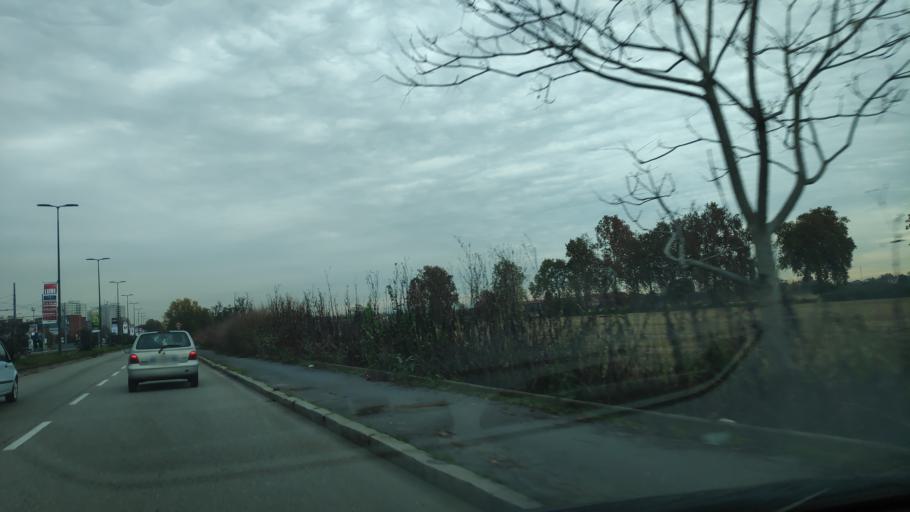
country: IT
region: Lombardy
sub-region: Citta metropolitana di Milano
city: Rozzano
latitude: 45.3967
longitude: 9.1735
